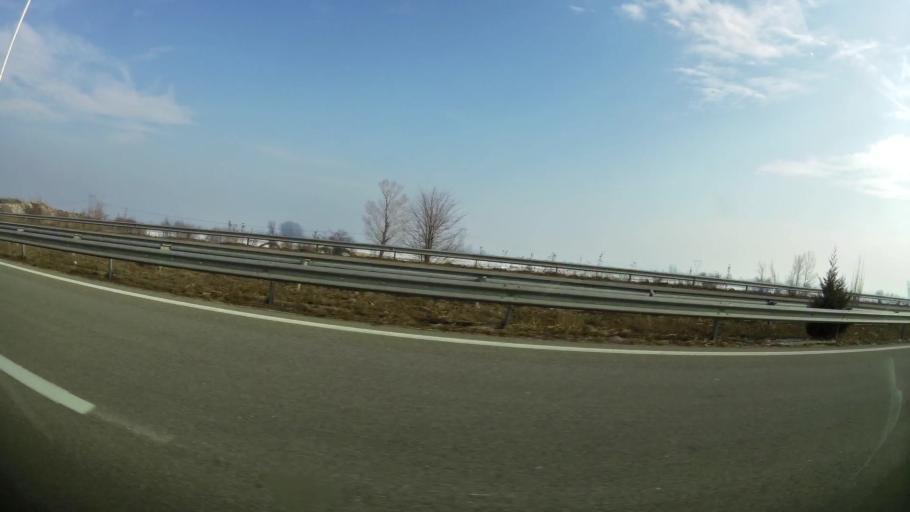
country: MK
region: Aracinovo
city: Arachinovo
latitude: 42.0058
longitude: 21.5349
